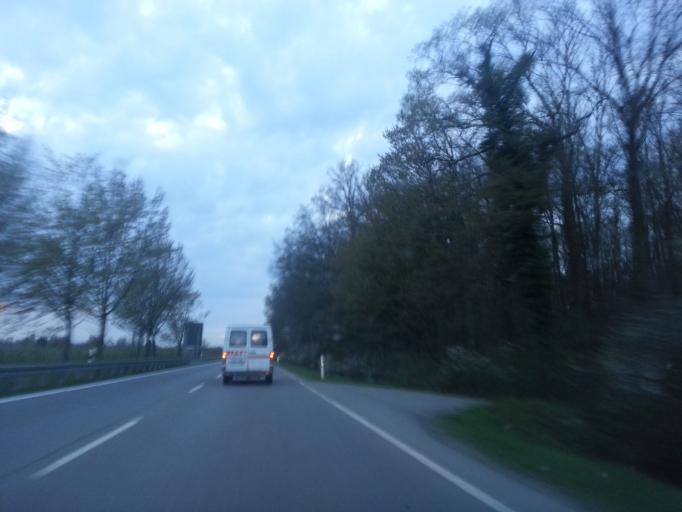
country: DE
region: Baden-Wuerttemberg
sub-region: Tuebingen Region
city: Eriskirch
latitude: 47.6361
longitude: 9.5220
